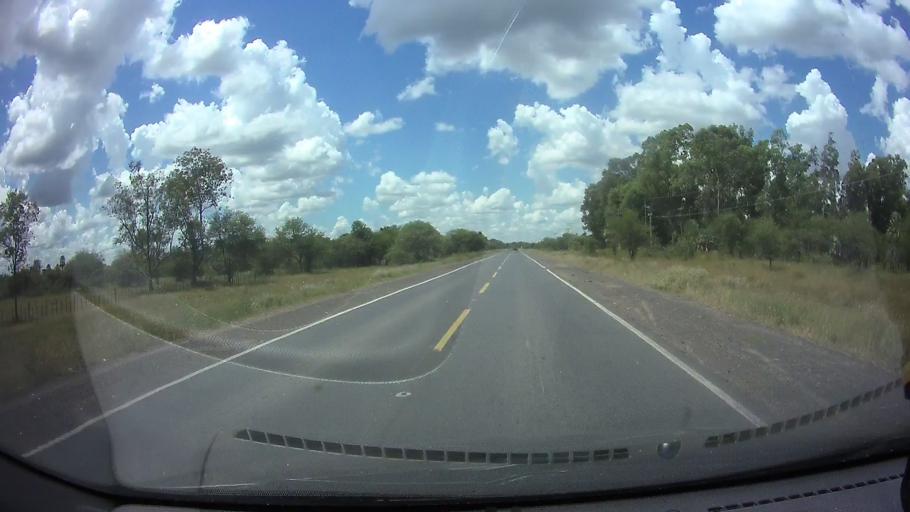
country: PY
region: Presidente Hayes
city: Nanawa
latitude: -25.2146
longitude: -57.6650
